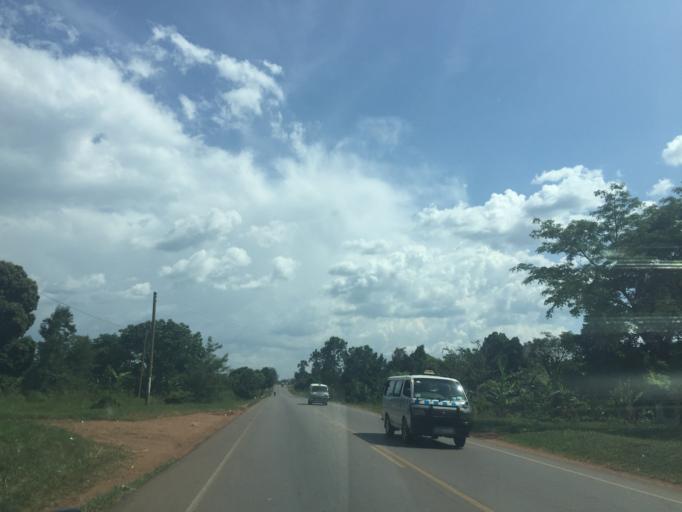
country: UG
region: Central Region
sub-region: Luwero District
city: Wobulenzi
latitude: 0.7720
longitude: 32.5120
